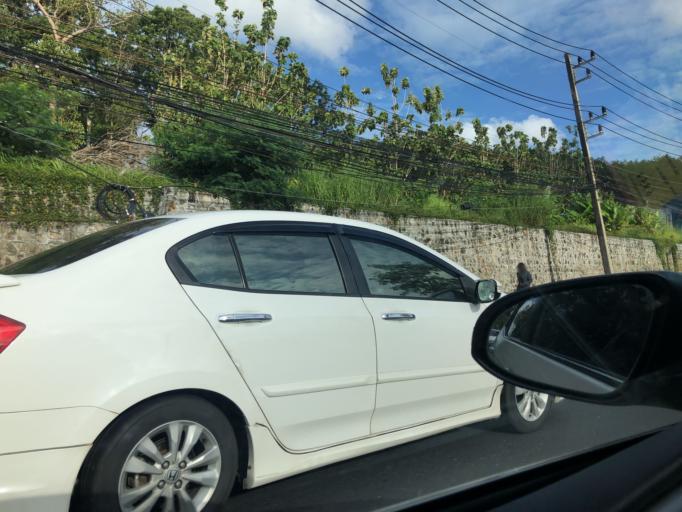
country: TH
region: Phuket
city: Ban Ko Kaeo
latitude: 7.9365
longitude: 98.3953
